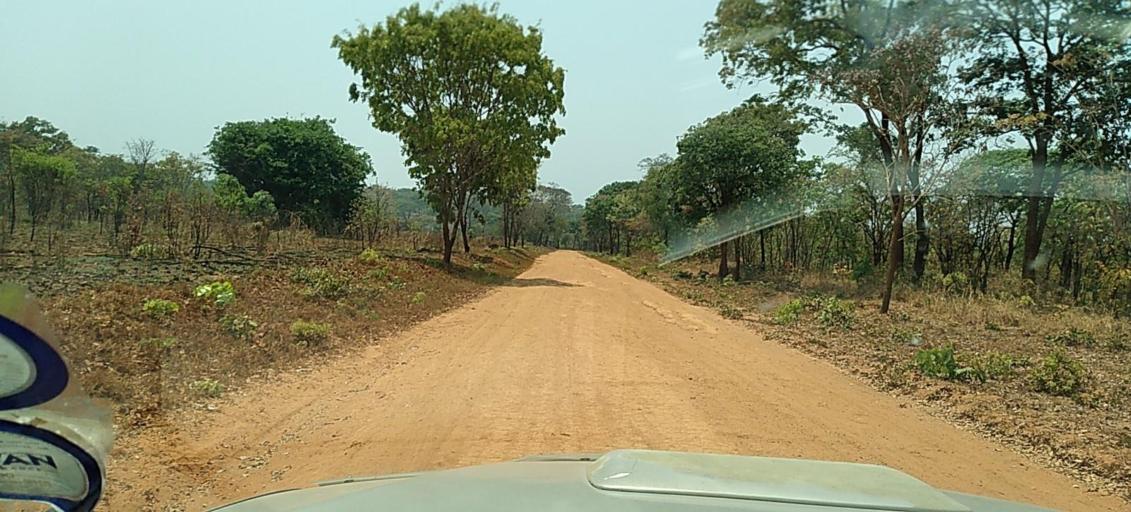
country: ZM
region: North-Western
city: Kasempa
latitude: -13.5459
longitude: 26.0383
